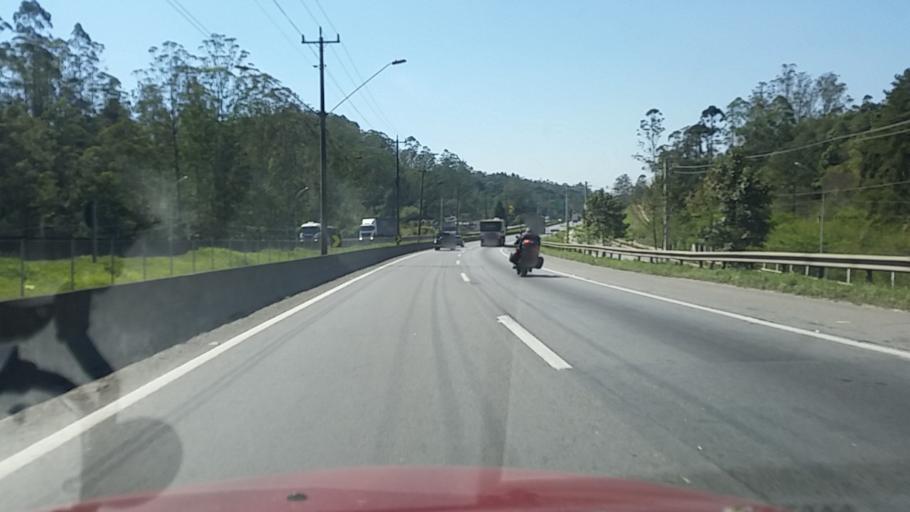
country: BR
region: Sao Paulo
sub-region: Sao Lourenco Da Serra
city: Sao Lourenco da Serra
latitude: -23.7780
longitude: -46.9157
